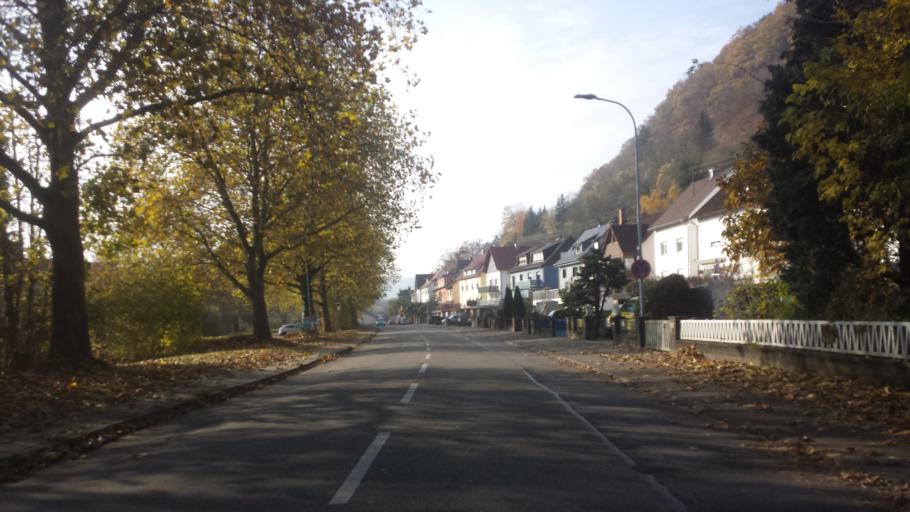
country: DE
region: Baden-Wuerttemberg
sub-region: Karlsruhe Region
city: Mosbach
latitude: 49.3483
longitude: 9.1281
